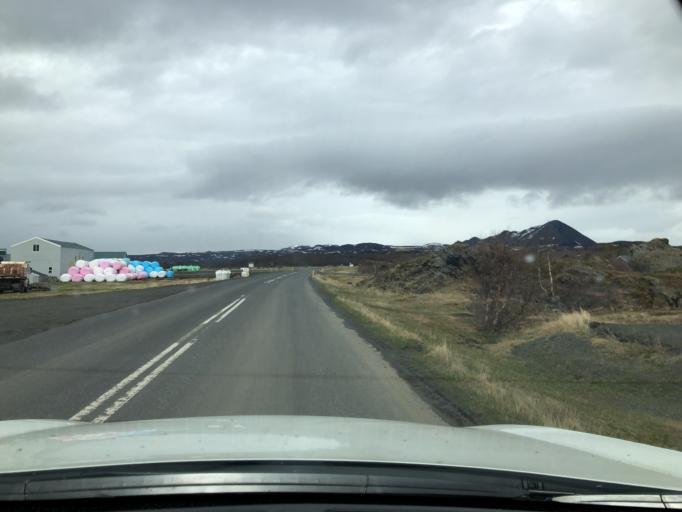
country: IS
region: Northeast
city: Laugar
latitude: 65.6235
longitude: -16.9192
